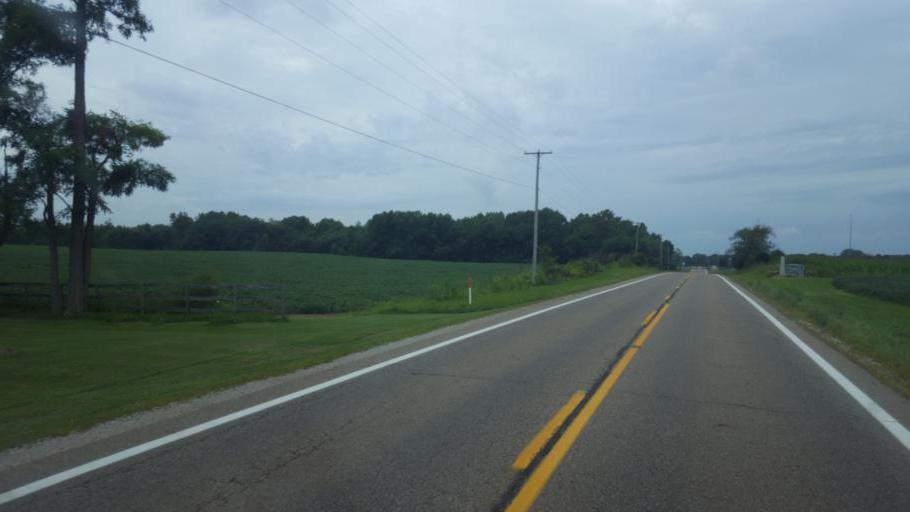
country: US
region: Ohio
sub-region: Morrow County
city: Mount Gilead
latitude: 40.5594
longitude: -82.8002
